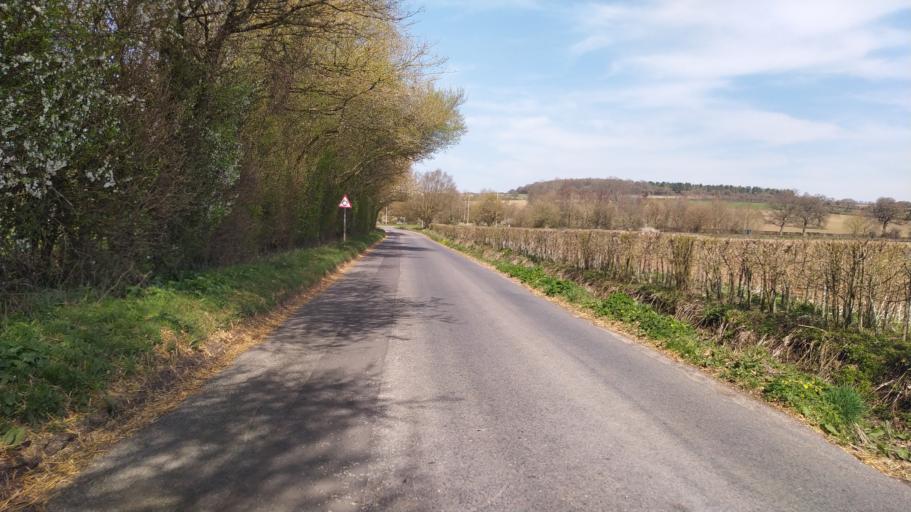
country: GB
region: England
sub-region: Hampshire
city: Four Marks
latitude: 51.0793
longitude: -1.1156
